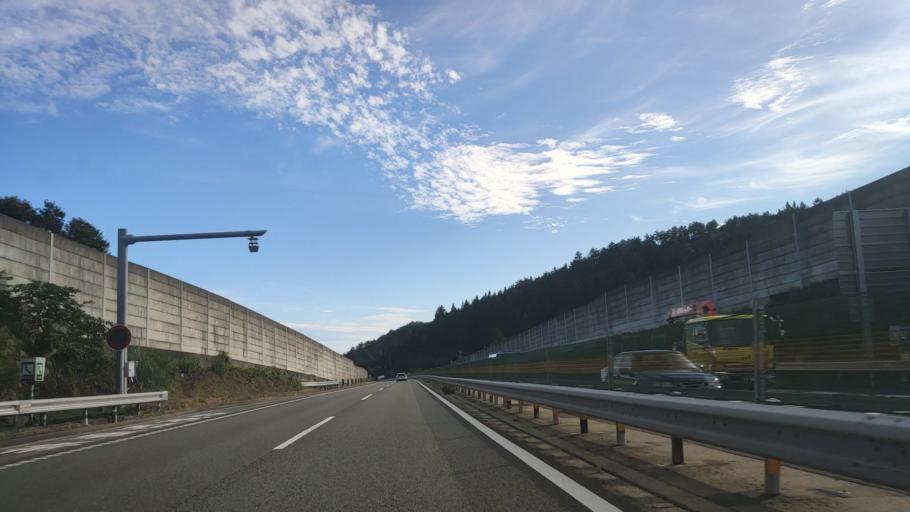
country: JP
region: Nagano
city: Ina
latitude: 35.6934
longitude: 137.9105
